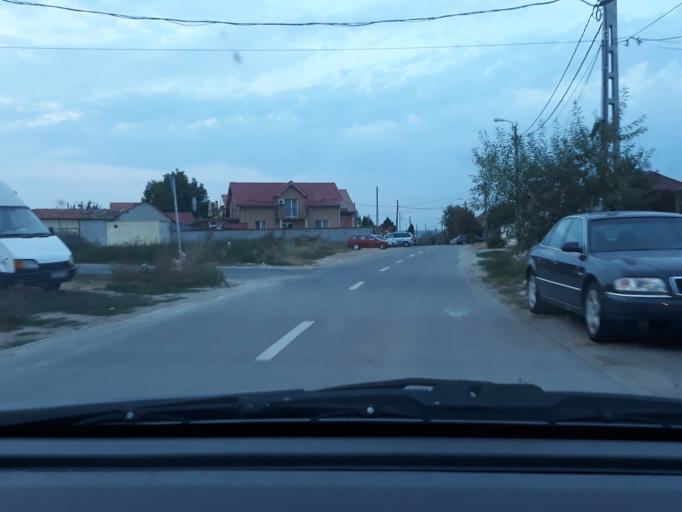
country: RO
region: Bihor
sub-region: Comuna Biharea
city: Oradea
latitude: 47.0264
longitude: 21.9354
